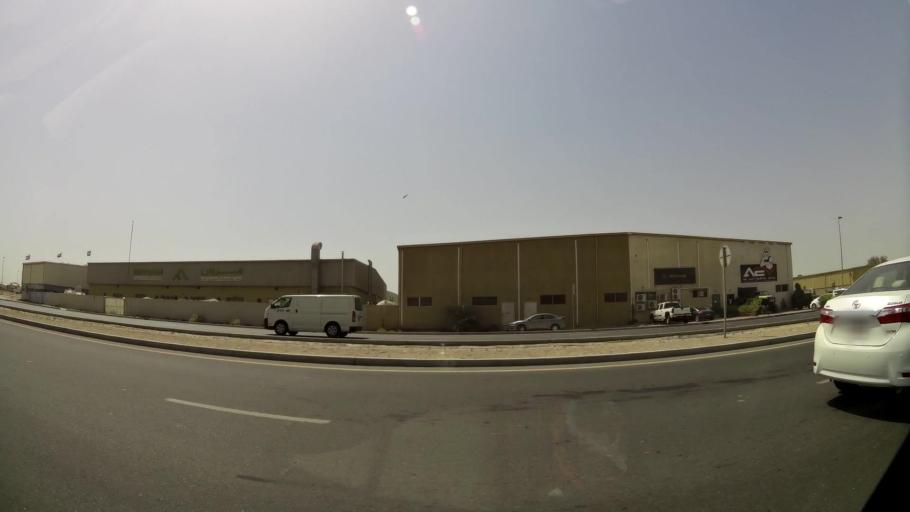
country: AE
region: Dubai
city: Dubai
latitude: 25.1586
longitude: 55.2382
